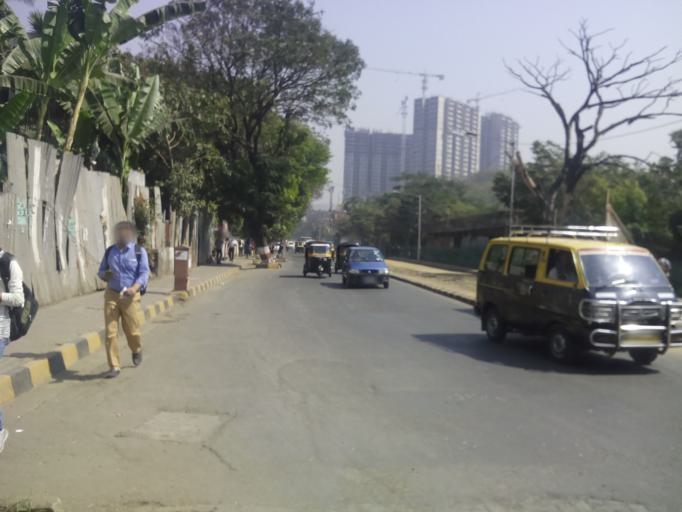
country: IN
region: Maharashtra
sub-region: Mumbai Suburban
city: Borivli
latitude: 19.2059
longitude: 72.8665
